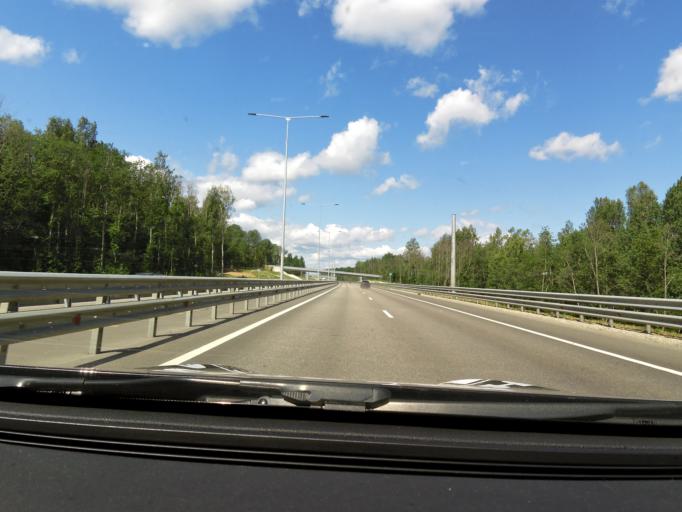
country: RU
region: Tverskaya
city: Vydropuzhsk
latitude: 57.3600
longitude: 34.6833
